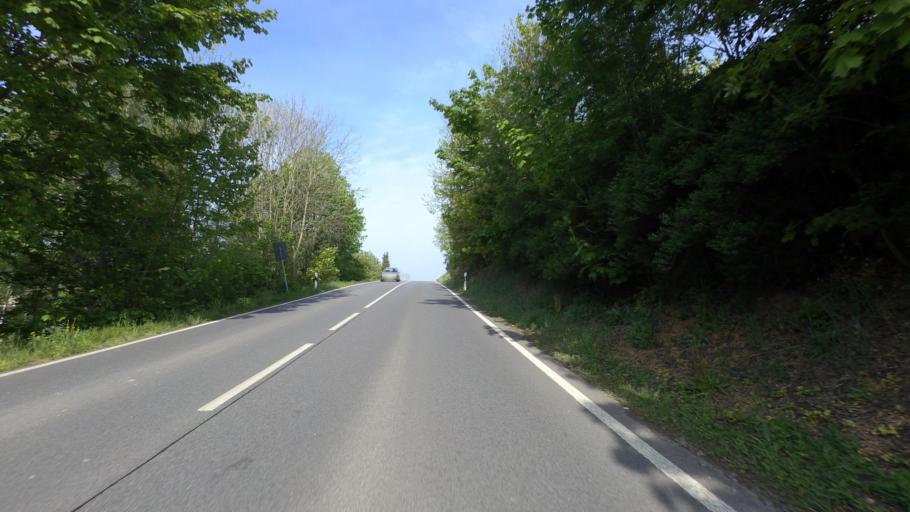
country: DE
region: Saxony
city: Stolpen
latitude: 51.0429
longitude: 14.1114
